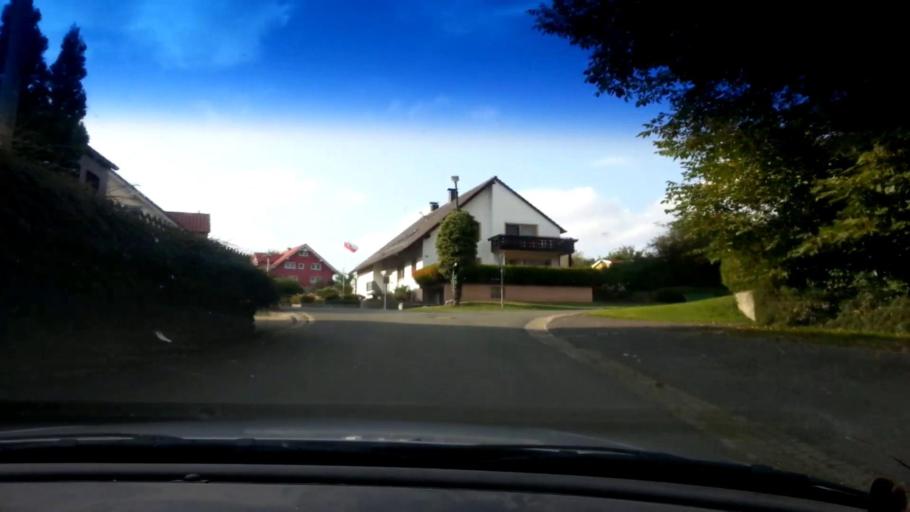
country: DE
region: Bavaria
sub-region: Upper Franconia
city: Schesslitz
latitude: 49.9923
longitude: 11.0456
